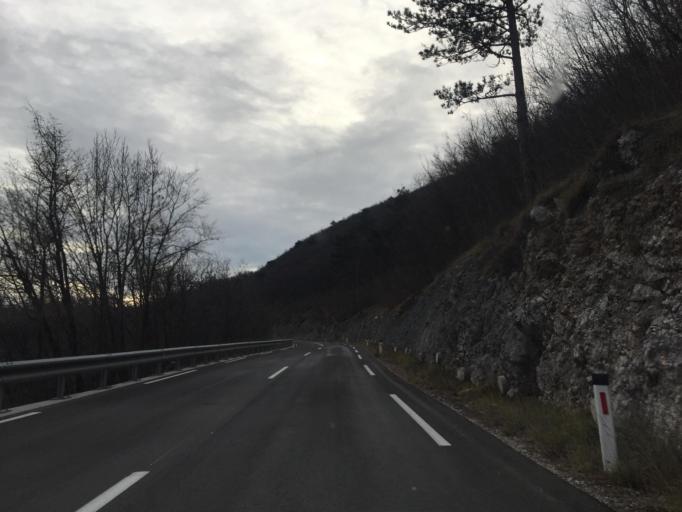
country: SI
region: Nova Gorica
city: Kromberk
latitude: 45.9846
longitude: 13.6787
